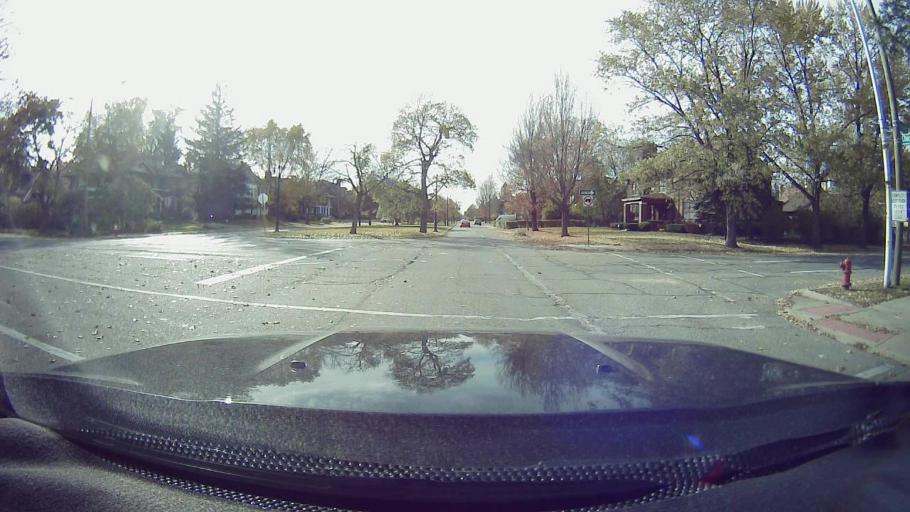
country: US
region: Michigan
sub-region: Wayne County
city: Highland Park
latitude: 42.3852
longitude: -83.0873
